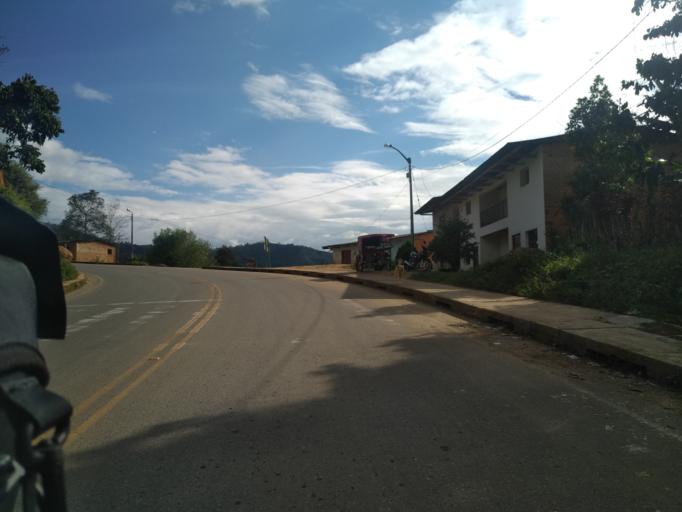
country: PE
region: Cajamarca
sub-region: Provincia de San Ignacio
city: San Ignacio
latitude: -5.0998
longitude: -79.0453
